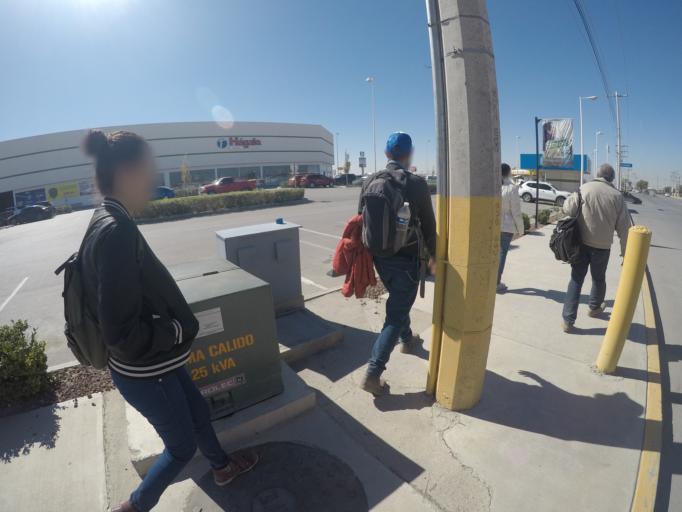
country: US
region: Texas
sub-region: El Paso County
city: Socorro
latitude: 31.6950
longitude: -106.3793
